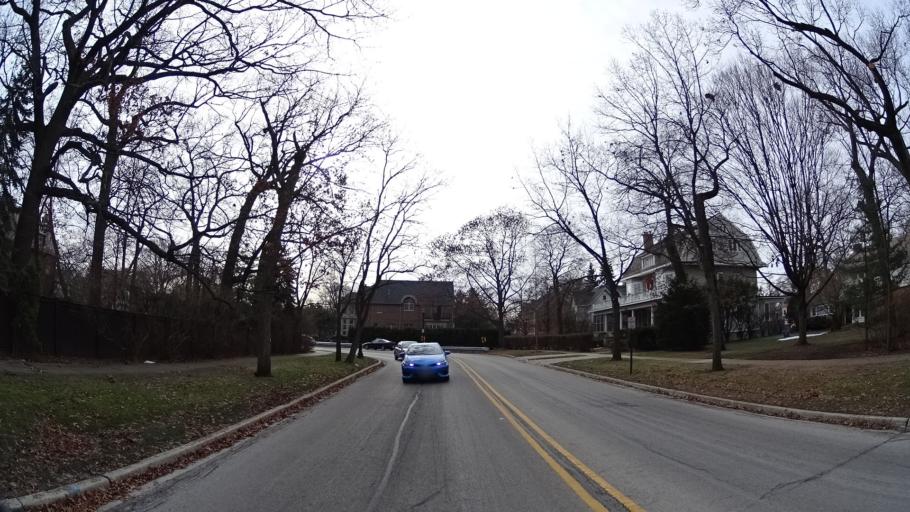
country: US
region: Illinois
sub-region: Cook County
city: Evanston
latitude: 42.0399
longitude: -87.6903
